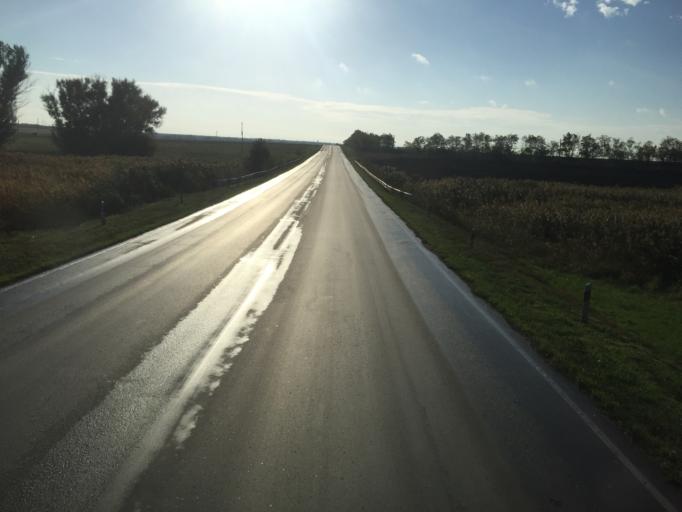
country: RU
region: Rostov
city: Mechetinskaya
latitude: 46.6722
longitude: 40.5313
